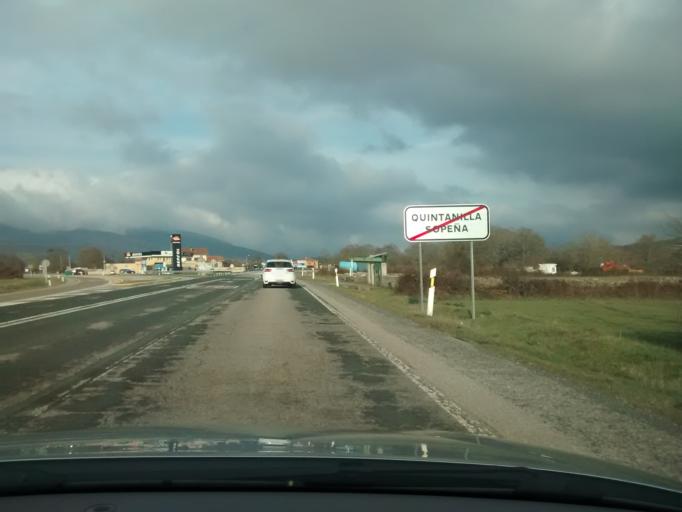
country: ES
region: Castille and Leon
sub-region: Provincia de Burgos
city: Espinosa de los Monteros
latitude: 43.0784
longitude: -3.4600
